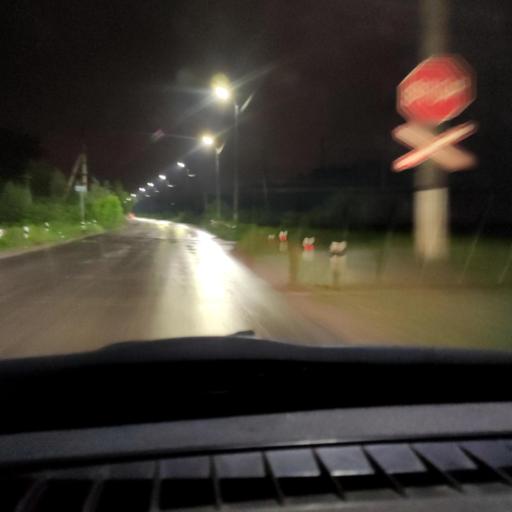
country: RU
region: Samara
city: Zhigulevsk
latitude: 53.4078
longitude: 49.4875
